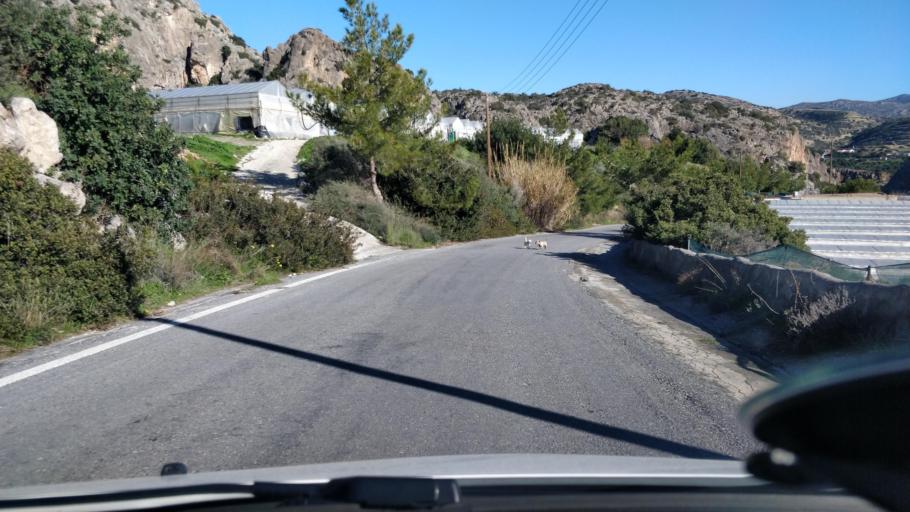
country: GR
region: Crete
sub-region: Nomos Lasithiou
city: Gra Liyia
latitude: 35.0381
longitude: 25.6686
